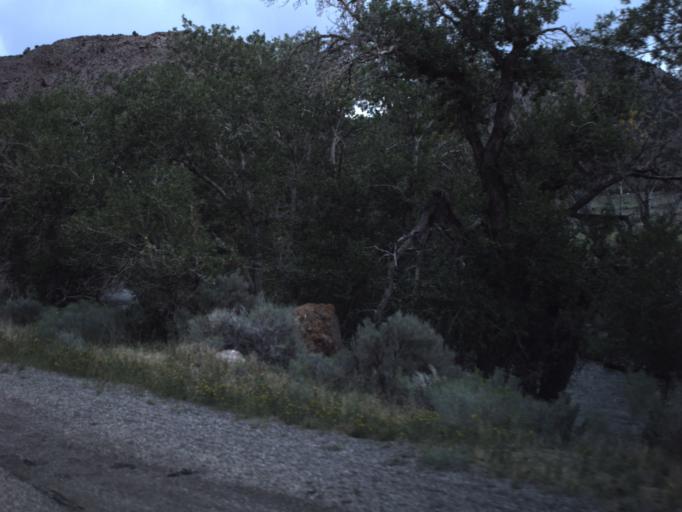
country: US
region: Utah
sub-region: Piute County
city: Junction
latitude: 38.1952
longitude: -112.1394
